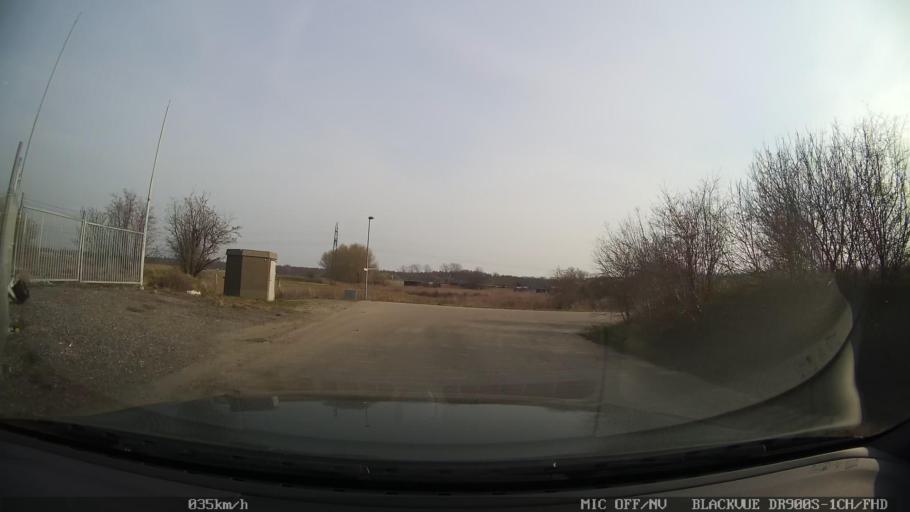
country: SE
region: Skane
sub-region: Ystads Kommun
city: Ystad
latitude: 55.4450
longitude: 13.8542
